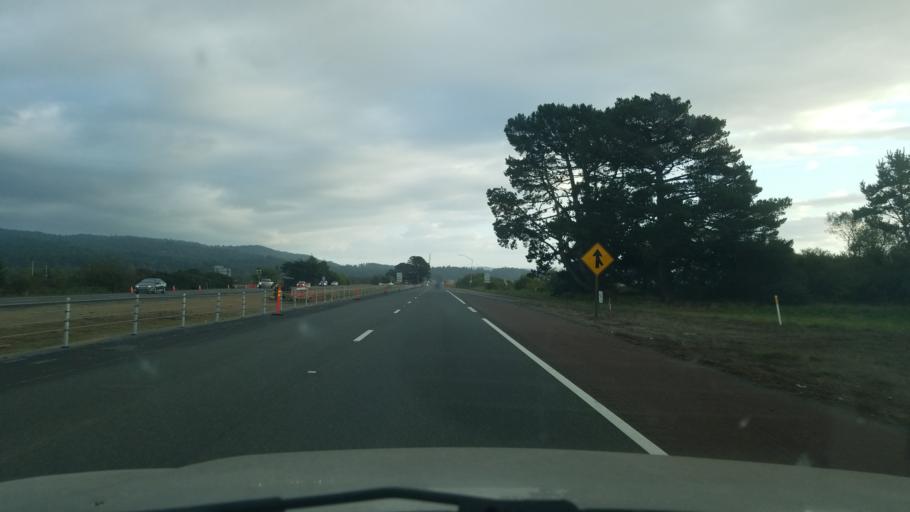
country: US
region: California
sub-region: Humboldt County
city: Arcata
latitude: 40.8511
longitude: -124.0821
